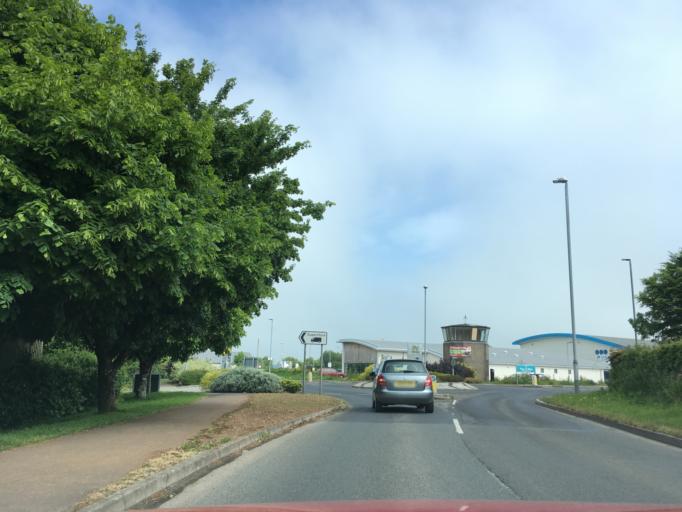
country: GB
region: England
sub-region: Devon
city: Dartmouth
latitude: 50.3472
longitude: -3.6029
